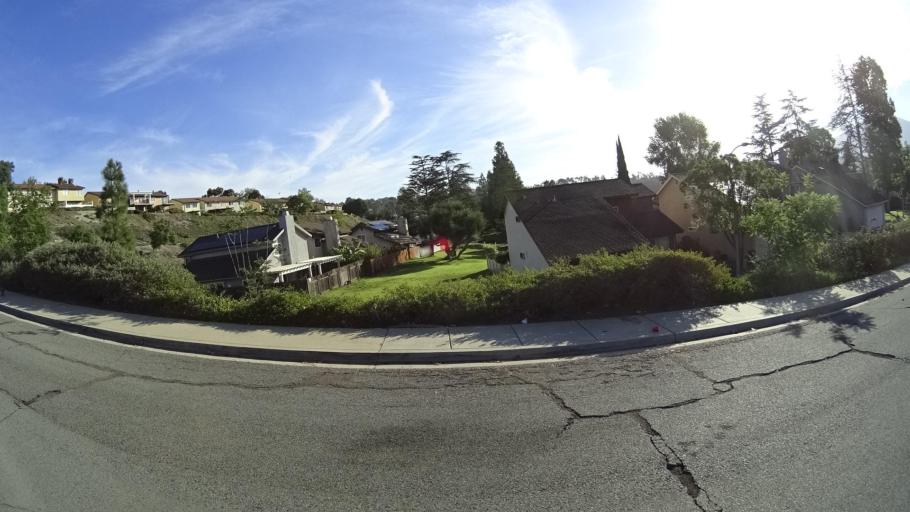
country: US
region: California
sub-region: San Diego County
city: Spring Valley
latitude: 32.7341
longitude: -116.9775
